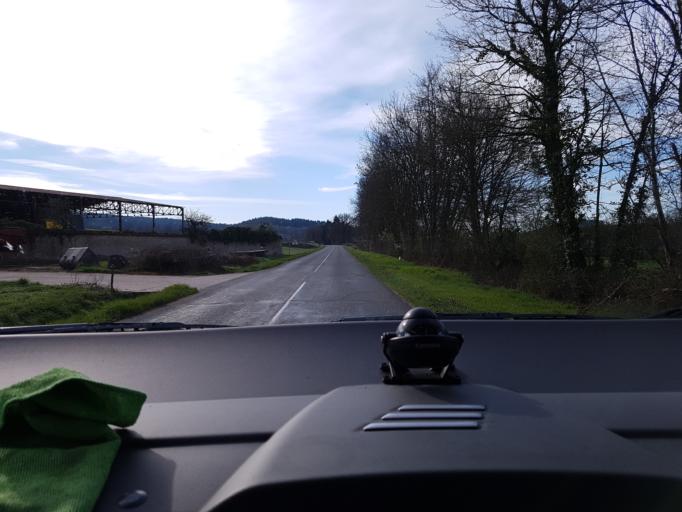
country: FR
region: Bourgogne
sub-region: Departement de Saone-et-Loire
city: Toulon-sur-Arroux
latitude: 46.7372
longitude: 4.1259
